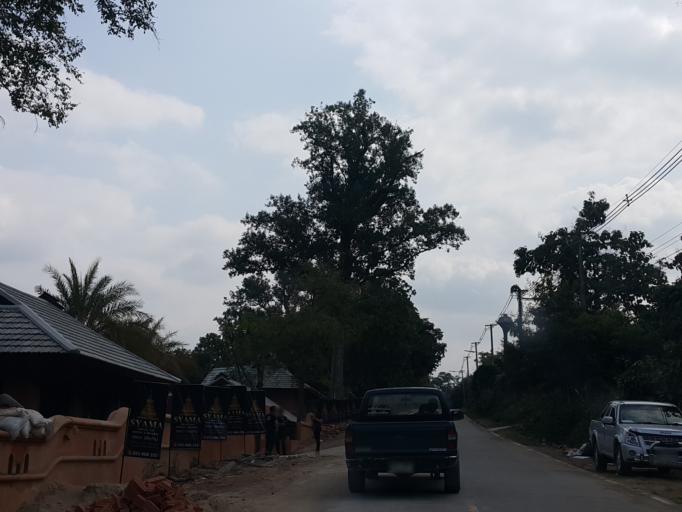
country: TH
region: Chiang Mai
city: Mae On
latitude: 18.8280
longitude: 99.2101
